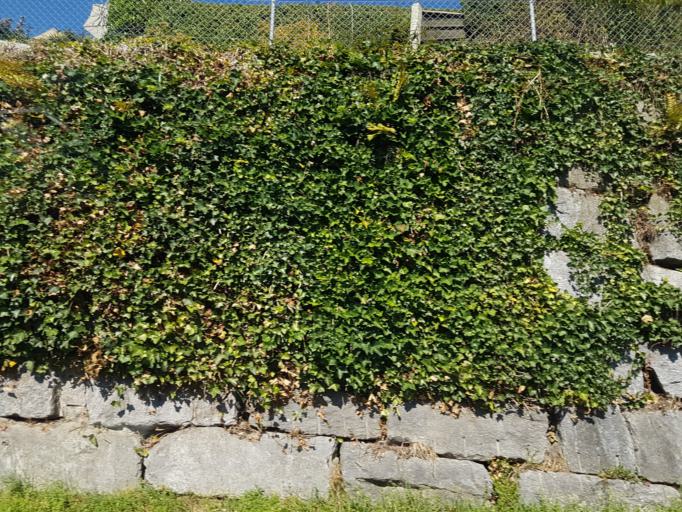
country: CH
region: Lucerne
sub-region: Lucerne-Land District
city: Udligenswil
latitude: 47.0856
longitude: 8.3994
